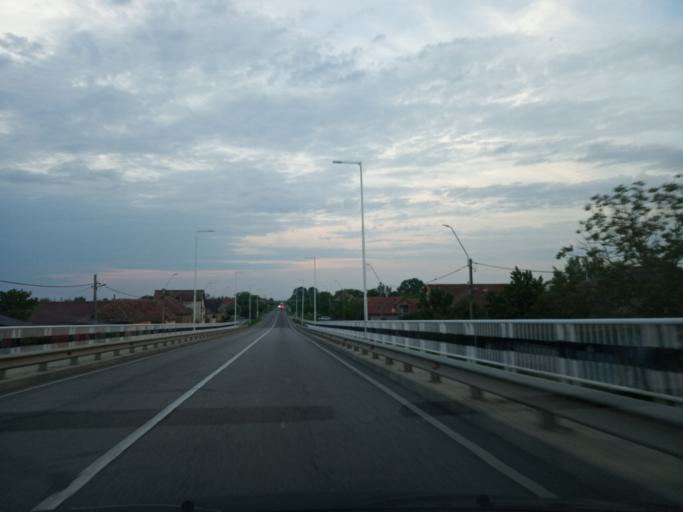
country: RO
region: Timis
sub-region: Comuna Voiteg
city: Voiteg
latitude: 45.4661
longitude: 21.2354
